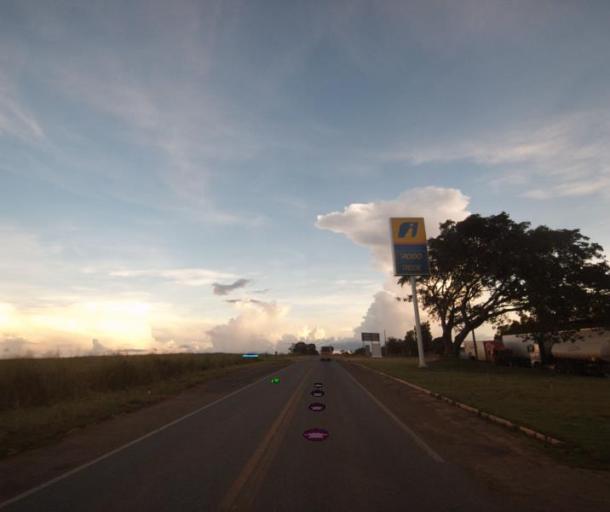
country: BR
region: Goias
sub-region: Uruacu
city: Uruacu
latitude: -14.4300
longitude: -49.1569
